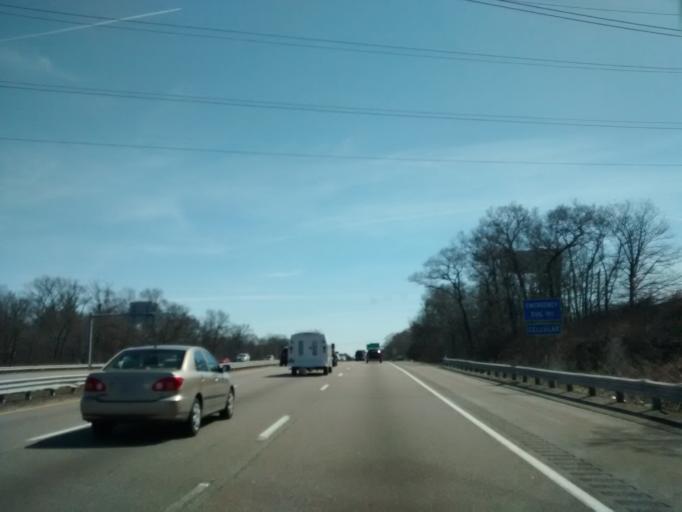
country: US
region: Massachusetts
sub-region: Norfolk County
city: Avon
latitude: 42.1459
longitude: -71.0668
